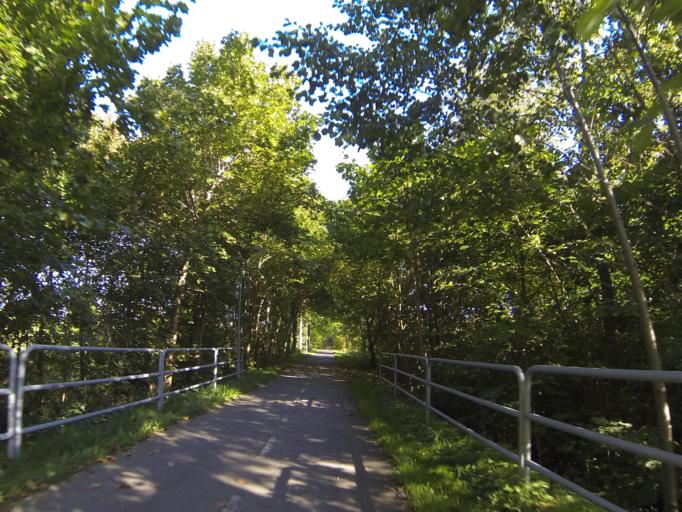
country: SE
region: Skane
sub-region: Lunds Kommun
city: Genarp
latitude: 55.7128
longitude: 13.3271
